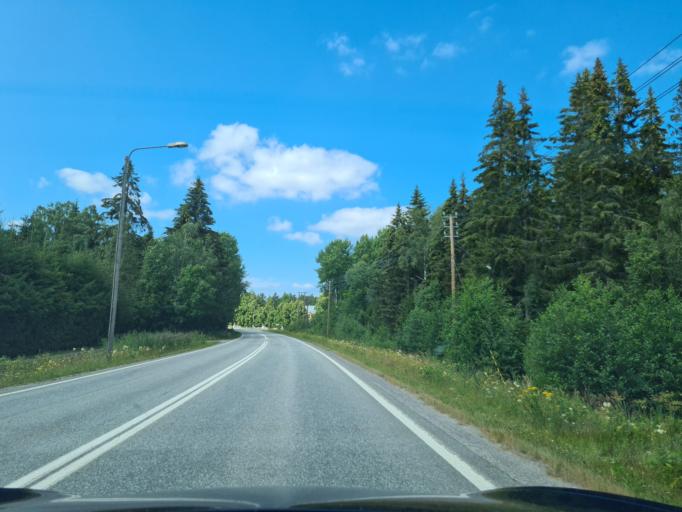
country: FI
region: Ostrobothnia
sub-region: Vaasa
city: Vaasa
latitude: 63.1908
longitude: 21.5632
